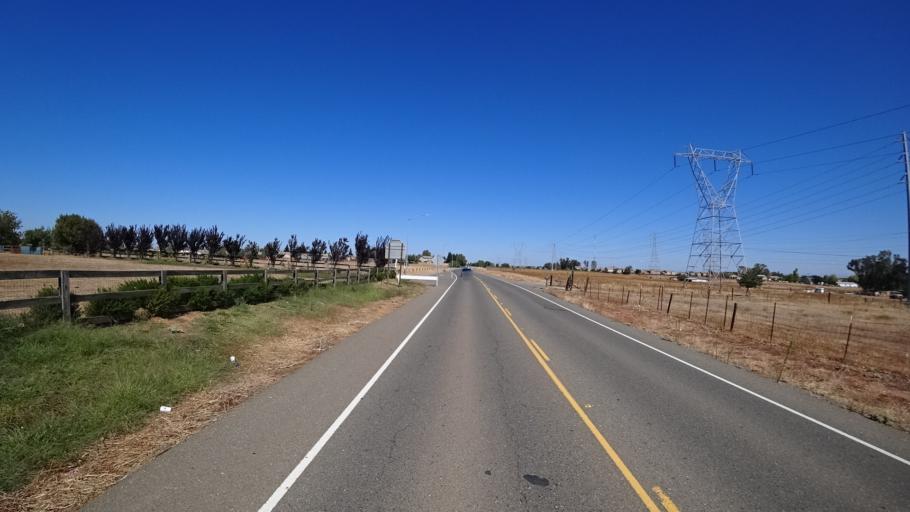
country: US
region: California
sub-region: Sacramento County
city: Vineyard
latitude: 38.4451
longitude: -121.3533
